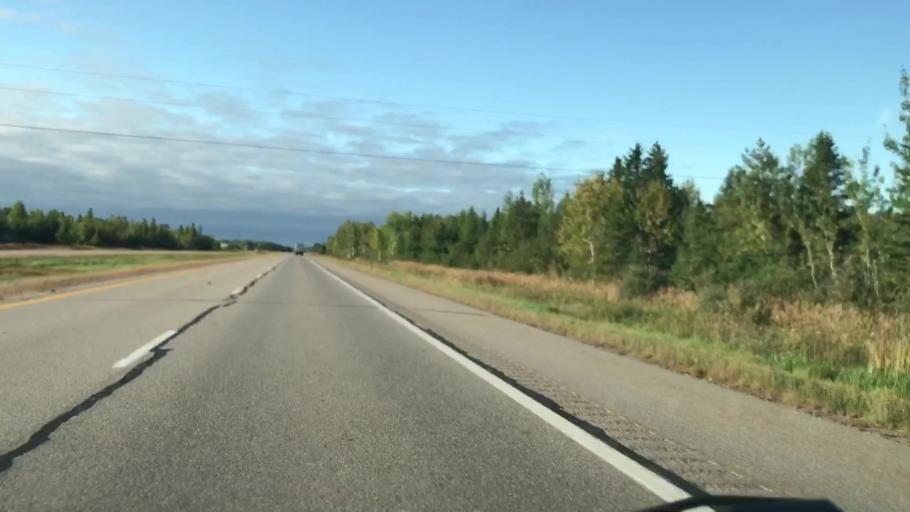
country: US
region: Michigan
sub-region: Chippewa County
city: Sault Ste. Marie
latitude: 46.4058
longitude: -84.4008
